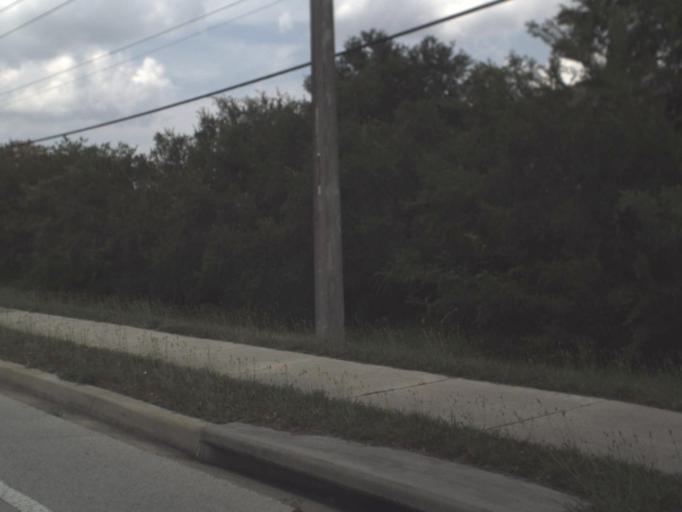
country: US
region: Florida
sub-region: Duval County
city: Atlantic Beach
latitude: 30.3179
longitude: -81.4774
